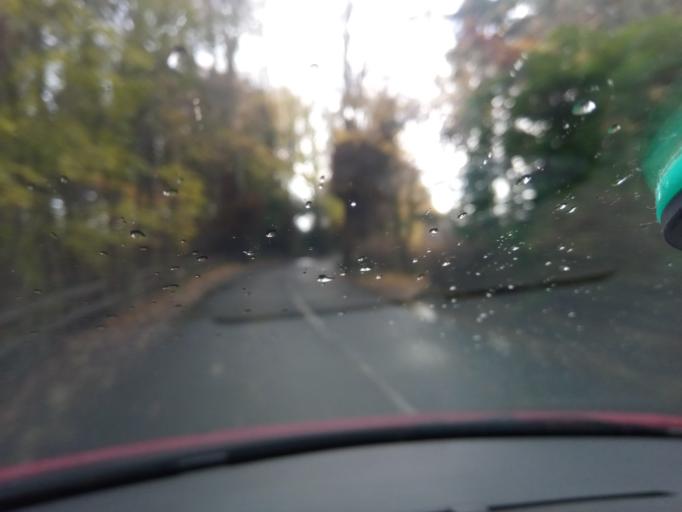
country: GB
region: England
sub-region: Northumberland
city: Birtley
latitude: 55.0993
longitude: -2.2249
